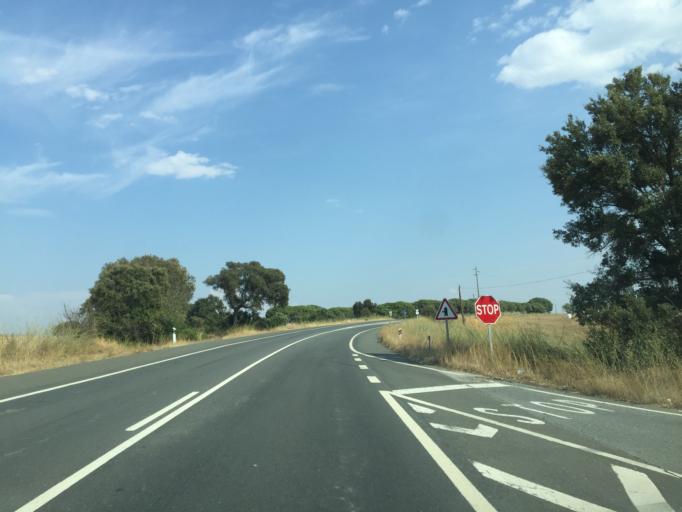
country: PT
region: Setubal
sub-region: Grandola
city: Grandola
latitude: 38.0106
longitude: -8.3806
